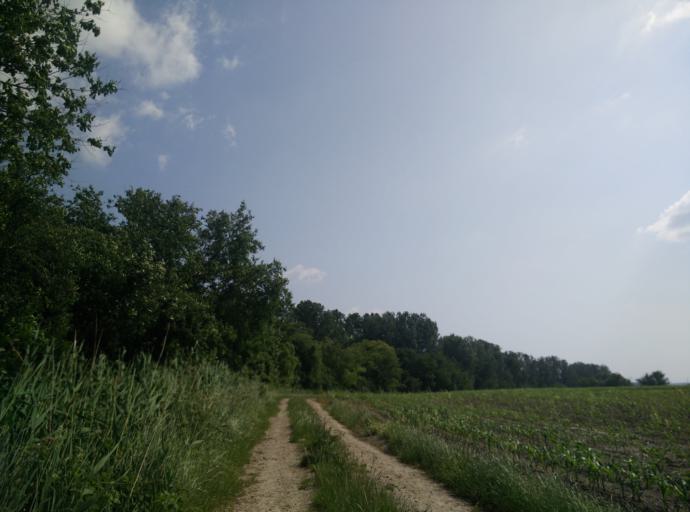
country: HU
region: Pest
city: Biatorbagy
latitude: 47.4739
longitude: 18.8042
